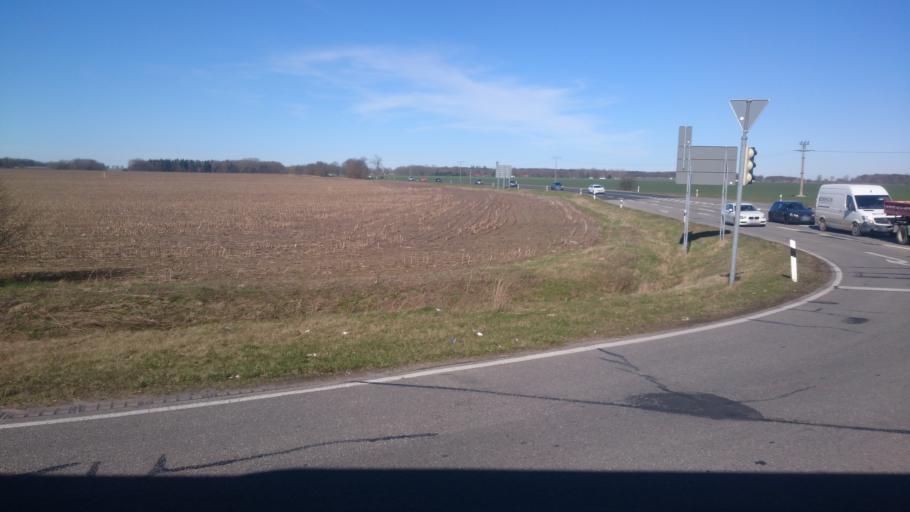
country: DE
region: Mecklenburg-Vorpommern
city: Jarmen
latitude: 53.9468
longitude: 13.3747
